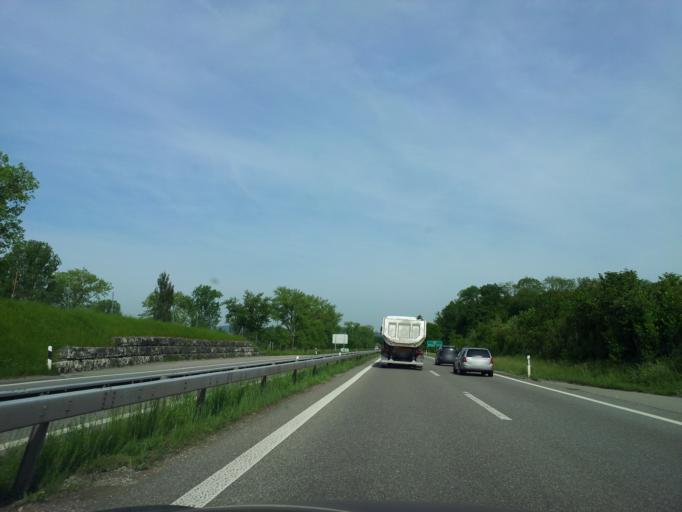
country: CH
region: Zurich
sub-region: Bezirk Buelach
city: Kloten / Freienberg (Chanzler-Chlini Chaseren)
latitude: 47.4657
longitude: 8.5686
